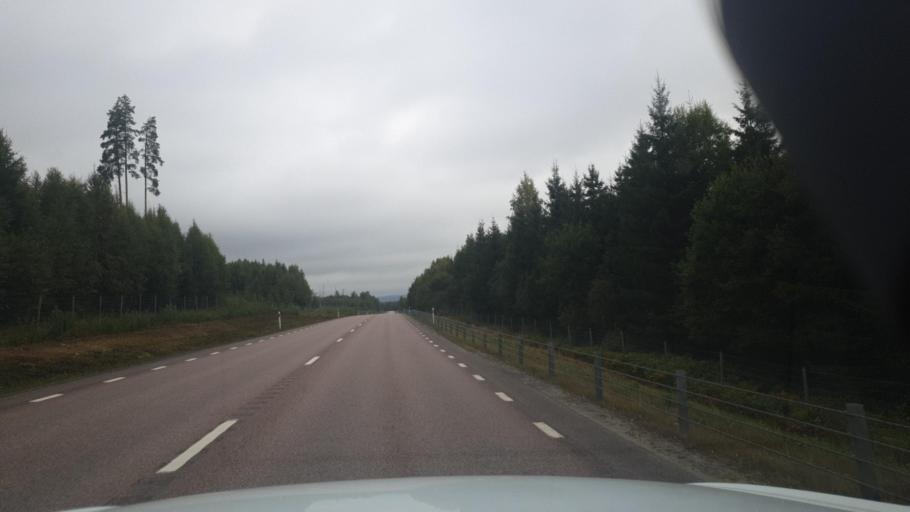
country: SE
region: Vaermland
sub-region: Sunne Kommun
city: Sunne
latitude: 59.7524
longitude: 13.1195
